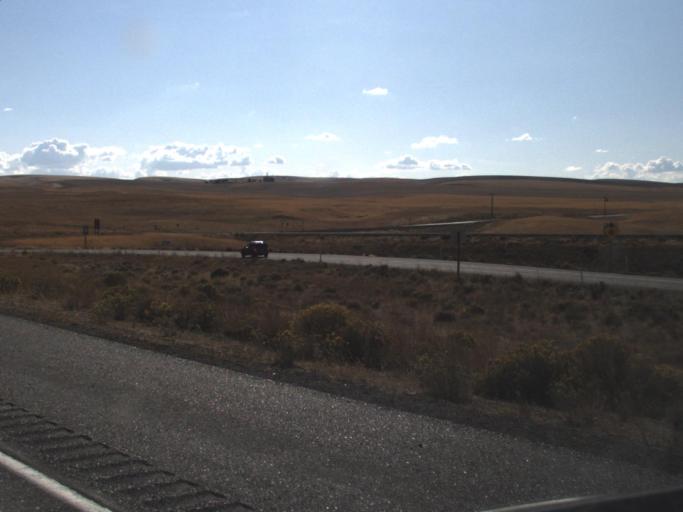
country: US
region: Washington
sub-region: Benton County
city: Highland
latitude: 46.1439
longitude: -119.2022
